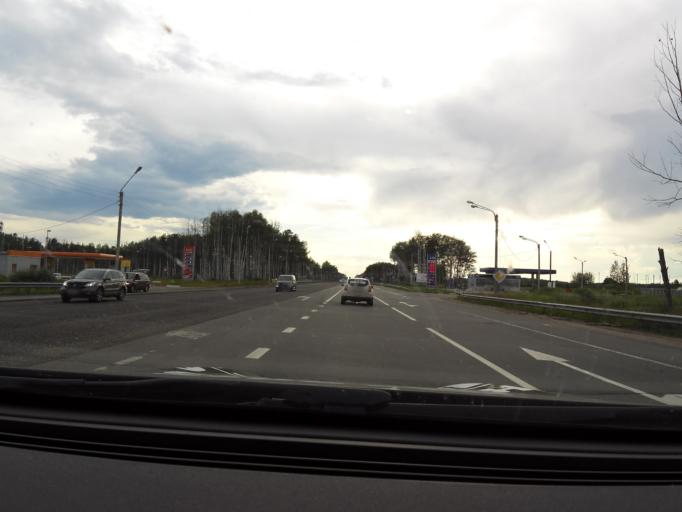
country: RU
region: Vladimir
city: Nikologory
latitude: 56.2366
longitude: 41.9436
